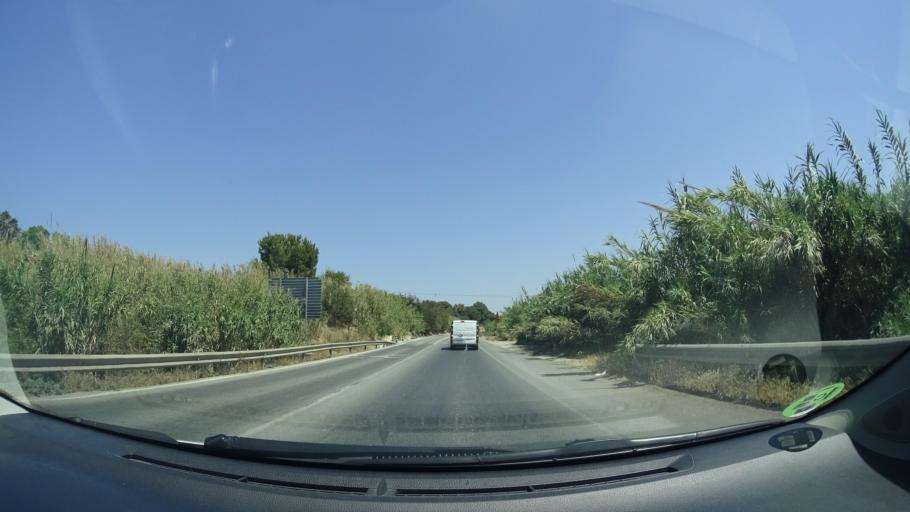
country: ES
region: Andalusia
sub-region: Provincia de Cadiz
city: Jerez de la Frontera
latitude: 36.6584
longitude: -6.0995
